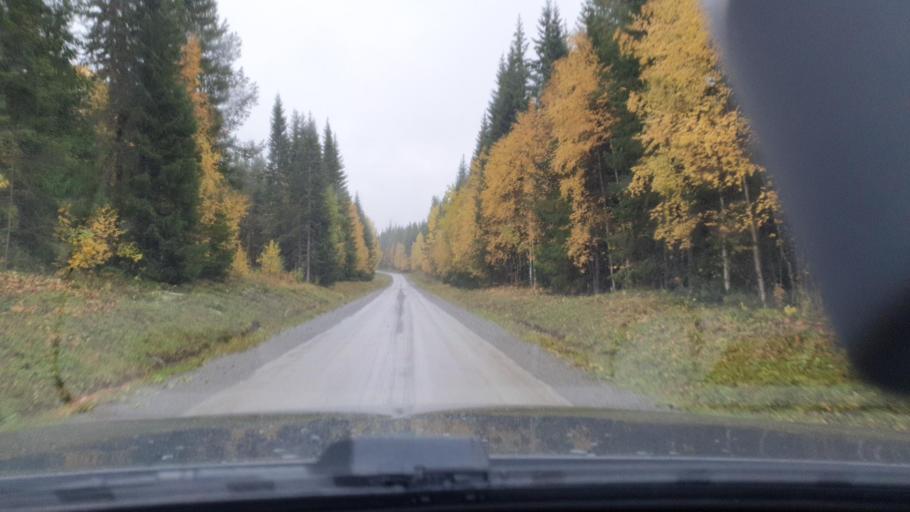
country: SE
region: Jaemtland
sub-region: Stroemsunds Kommun
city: Stroemsund
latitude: 63.5340
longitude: 15.6107
